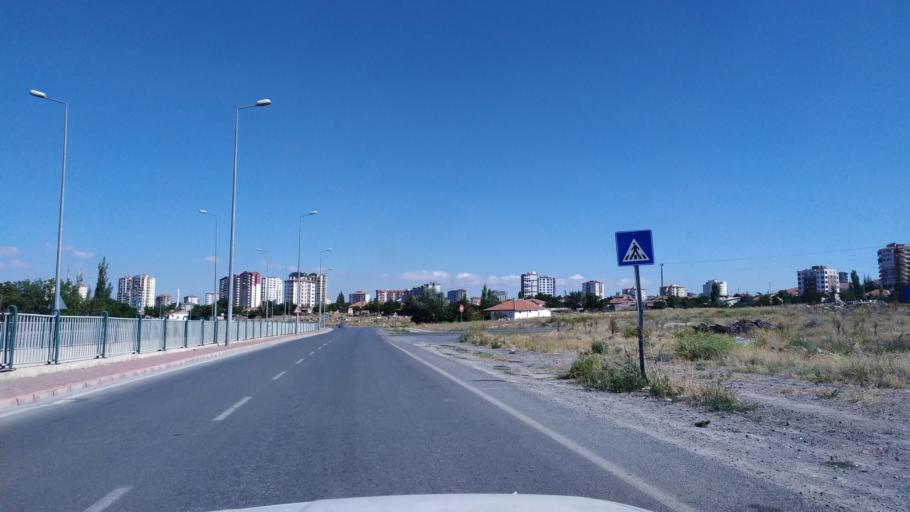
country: TR
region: Kayseri
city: Talas
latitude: 38.7312
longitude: 35.5493
